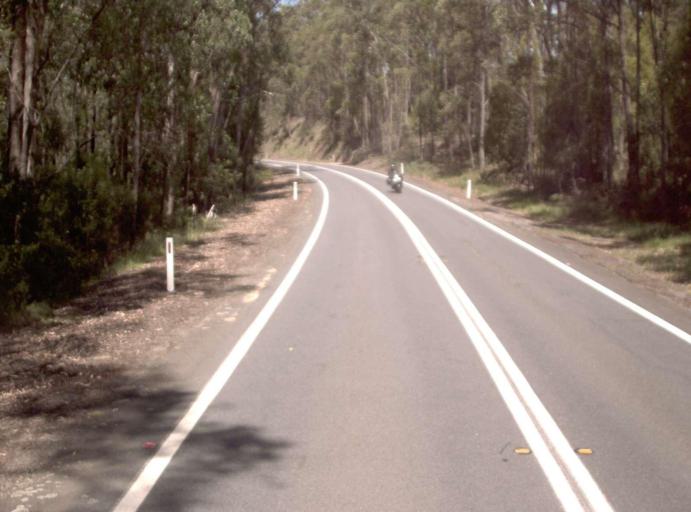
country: AU
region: New South Wales
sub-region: Bombala
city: Bombala
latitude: -37.5848
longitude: 148.9485
